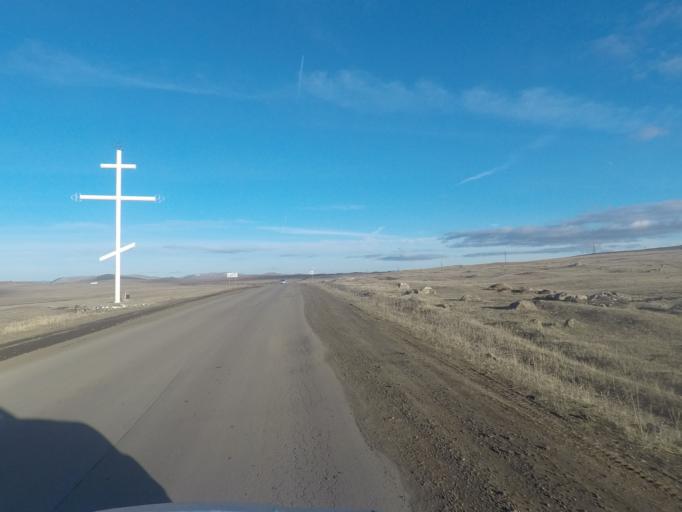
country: GE
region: Kvemo Kartli
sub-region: Tsalka
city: Tsalka
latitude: 41.5985
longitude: 44.0191
